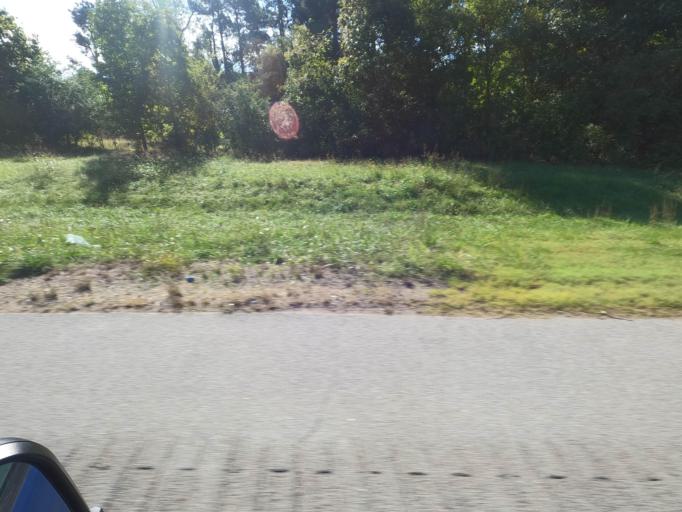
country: US
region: Tennessee
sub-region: Shelby County
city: Lakeland
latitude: 35.3093
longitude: -89.7821
